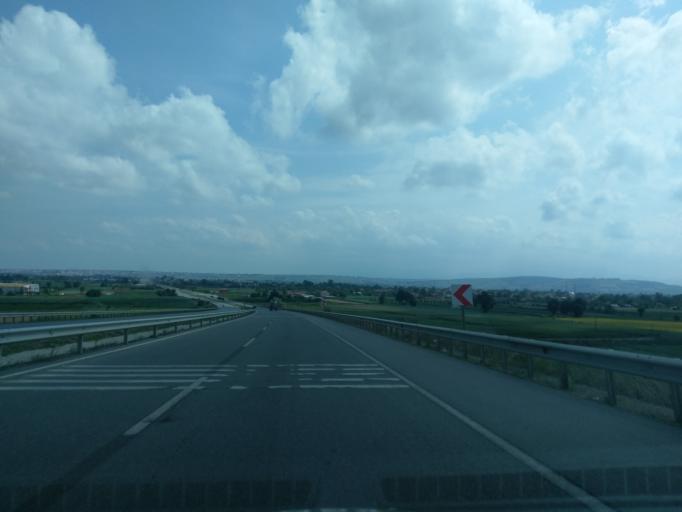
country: TR
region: Samsun
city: Bafra
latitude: 41.5811
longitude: 35.8447
